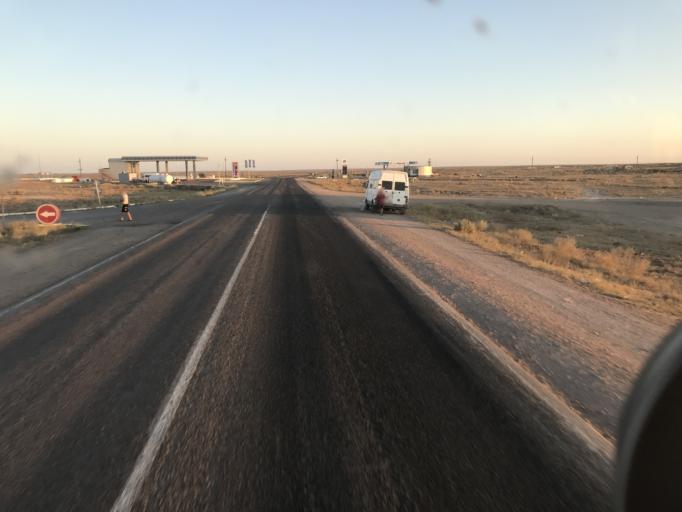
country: KZ
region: Qaraghandy
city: Saryshaghan
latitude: 46.0216
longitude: 73.5914
